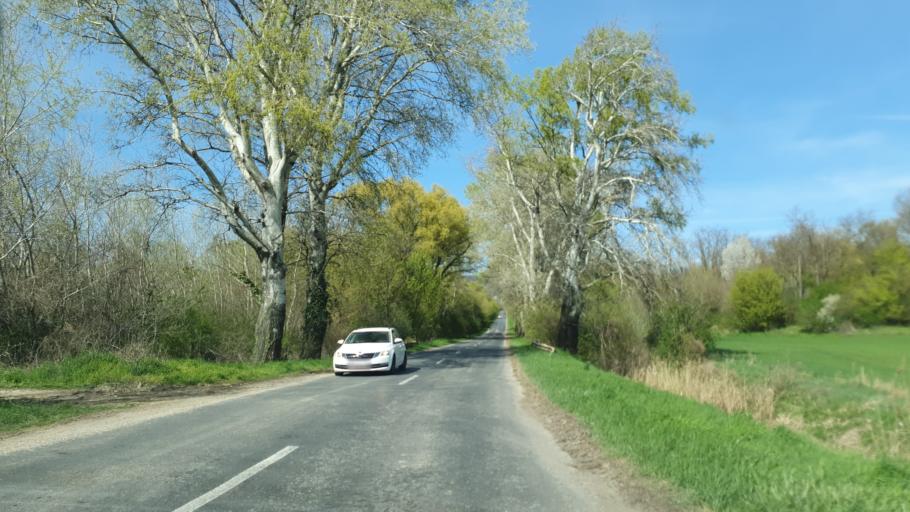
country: HU
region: Fejer
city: Bodajk
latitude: 47.3367
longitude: 18.2560
